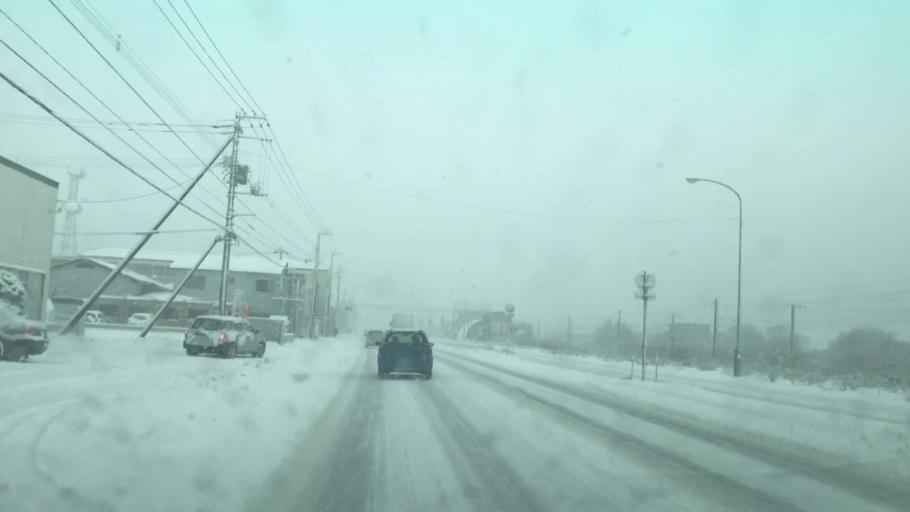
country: JP
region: Hokkaido
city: Muroran
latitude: 42.3862
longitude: 141.0787
